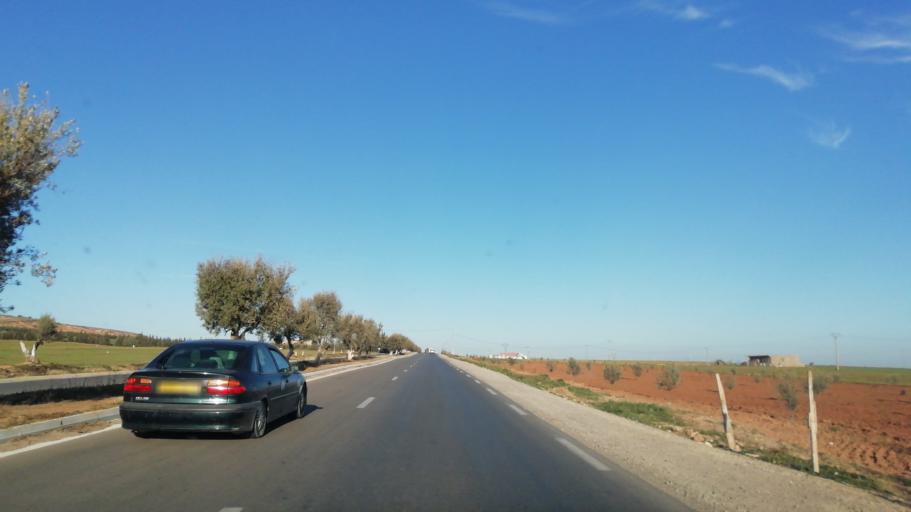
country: DZ
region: Mascara
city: Bou Hanifia el Hamamat
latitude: 35.3385
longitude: 0.0457
